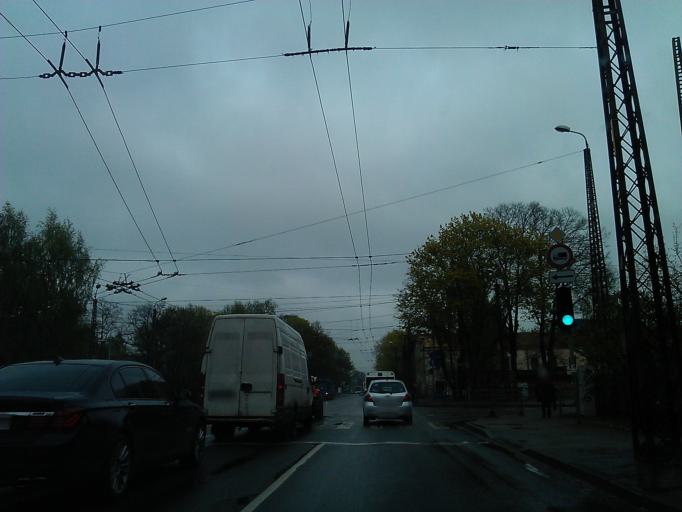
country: LV
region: Riga
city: Riga
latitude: 56.9510
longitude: 24.1727
